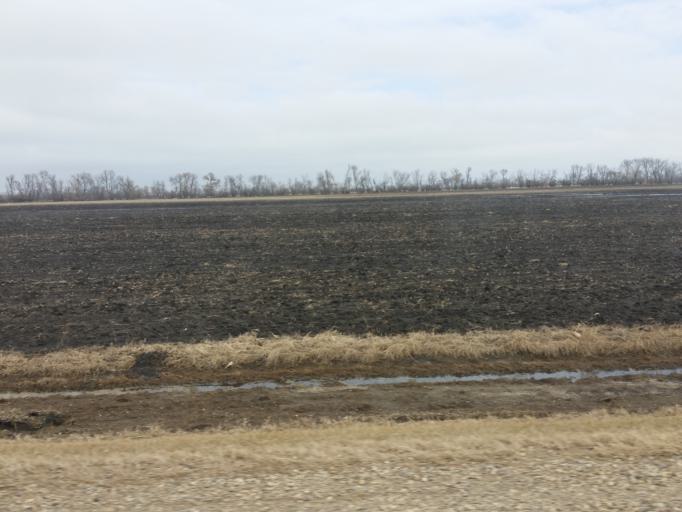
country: US
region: North Dakota
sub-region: Walsh County
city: Grafton
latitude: 48.4225
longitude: -97.3212
